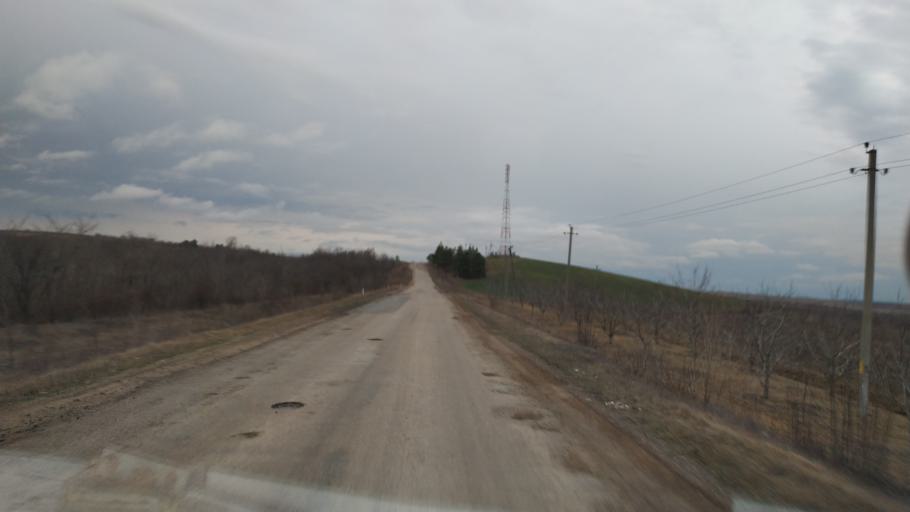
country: MD
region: Causeni
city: Causeni
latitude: 46.6201
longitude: 29.3946
